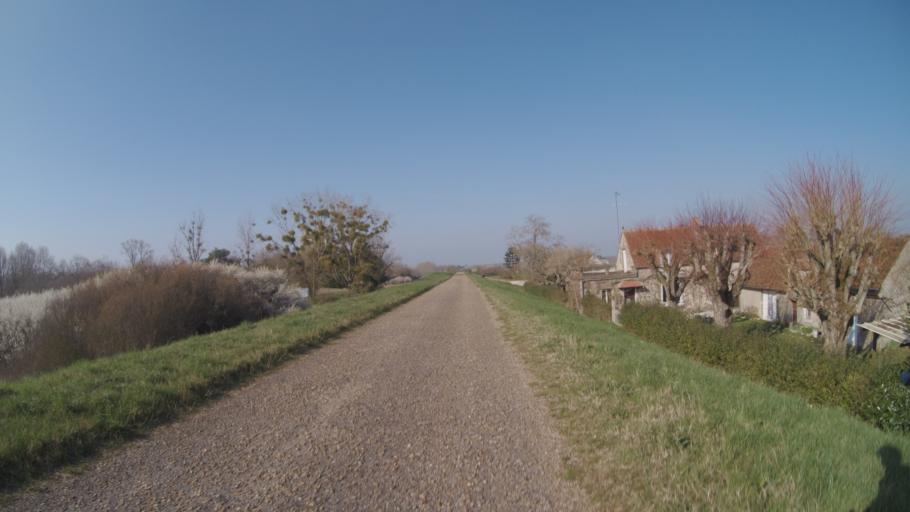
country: FR
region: Centre
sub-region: Departement du Loiret
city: Sandillon
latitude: 47.8677
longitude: 2.0371
